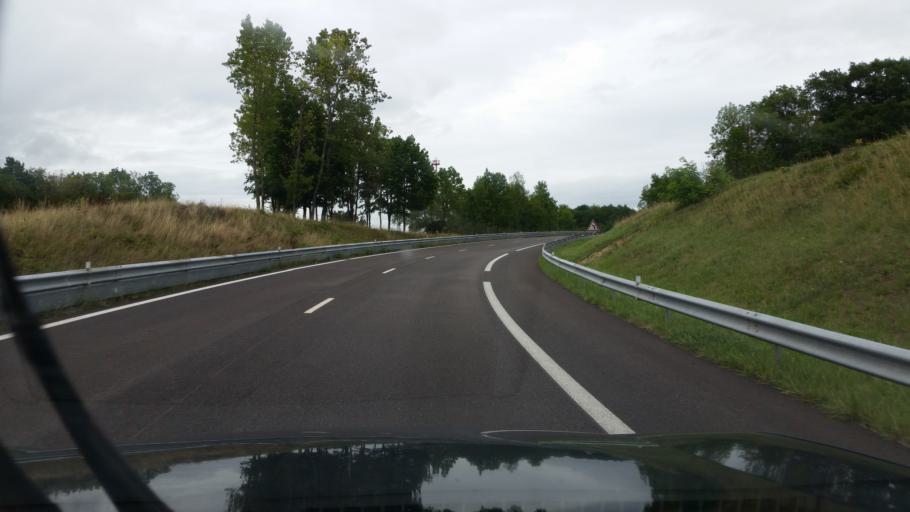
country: FR
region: Lorraine
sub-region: Departement de Meurthe-et-Moselle
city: Dommartin-les-Toul
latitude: 48.6507
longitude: 5.8811
